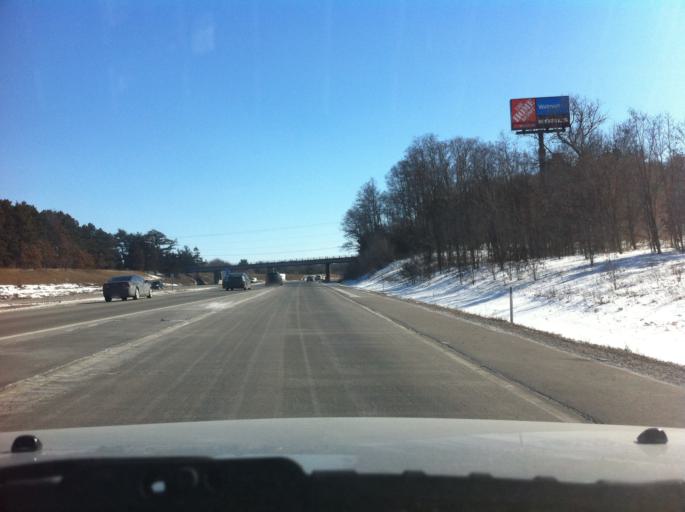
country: US
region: Wisconsin
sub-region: Sauk County
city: Lake Delton
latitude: 43.5754
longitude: -89.8014
